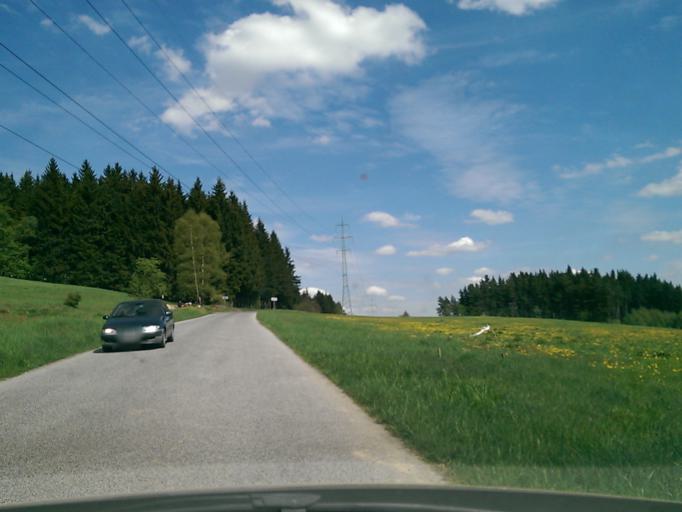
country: CZ
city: Pencin
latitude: 50.6828
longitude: 15.2176
